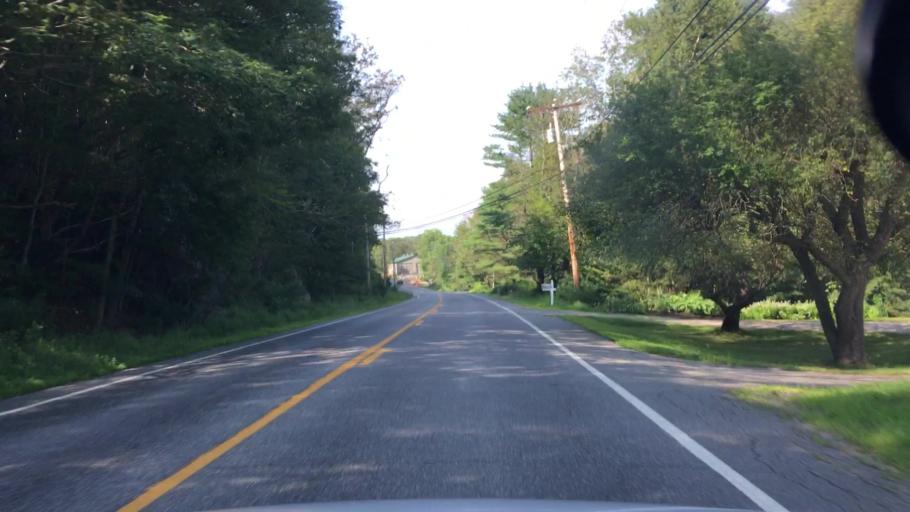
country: US
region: Maine
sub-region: Cumberland County
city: Harpswell Center
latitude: 43.8271
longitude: -69.9182
